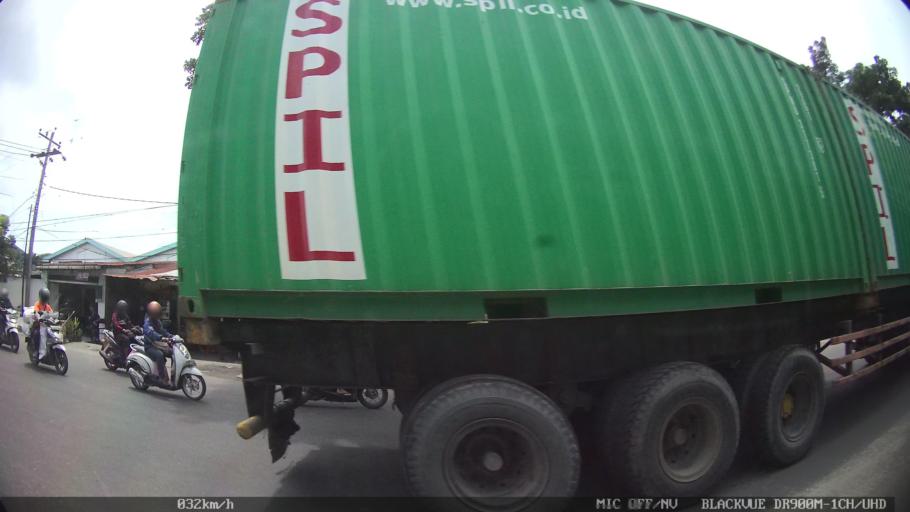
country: ID
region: North Sumatra
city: Labuhan Deli
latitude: 3.6583
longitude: 98.6652
